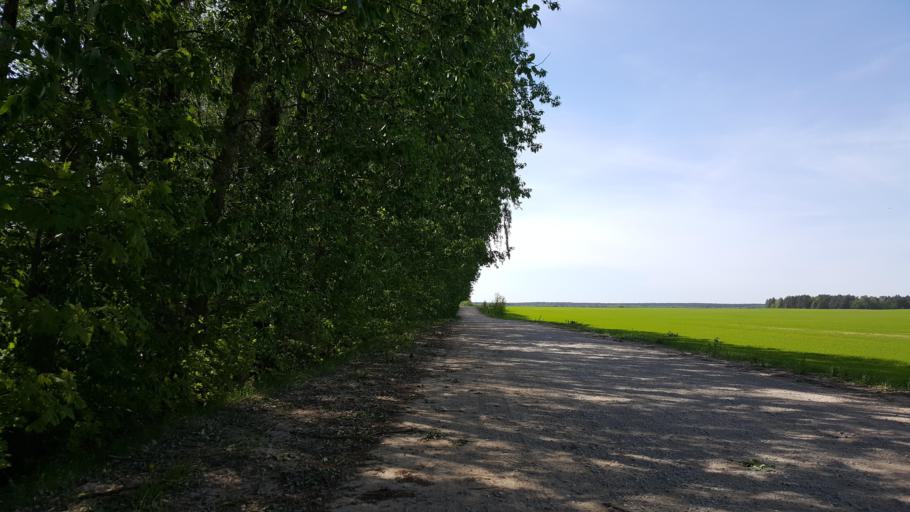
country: BY
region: Brest
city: Zhabinka
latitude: 52.3098
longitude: 24.0691
